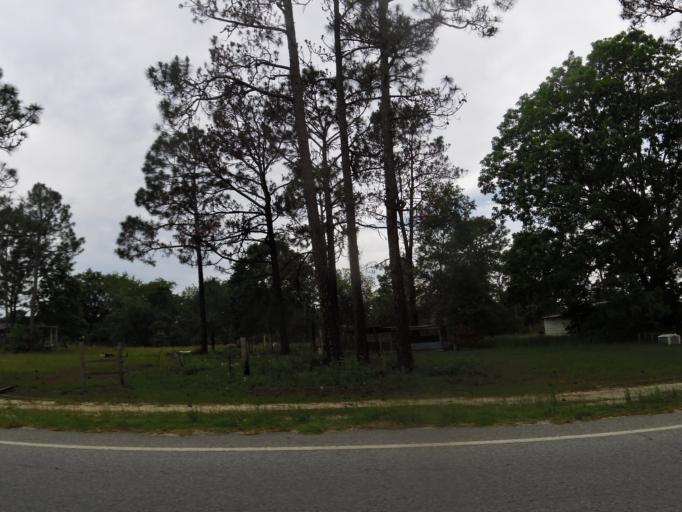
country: US
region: Georgia
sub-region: Emanuel County
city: Twin City
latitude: 32.4815
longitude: -82.2441
